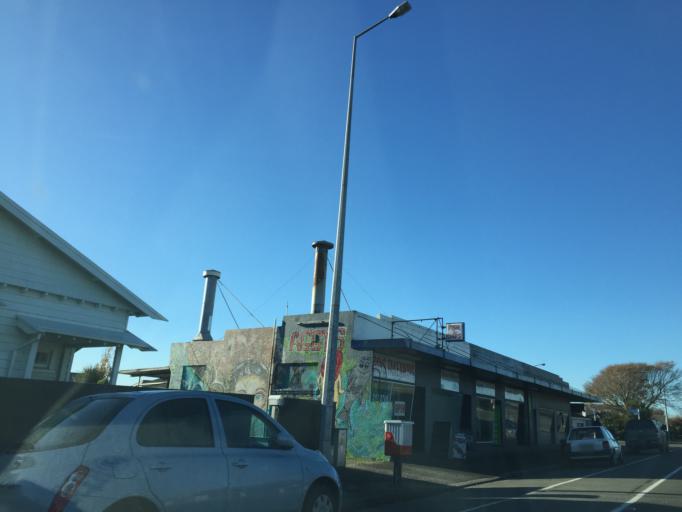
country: NZ
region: Southland
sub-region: Invercargill City
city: Invercargill
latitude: -46.4022
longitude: 168.3686
